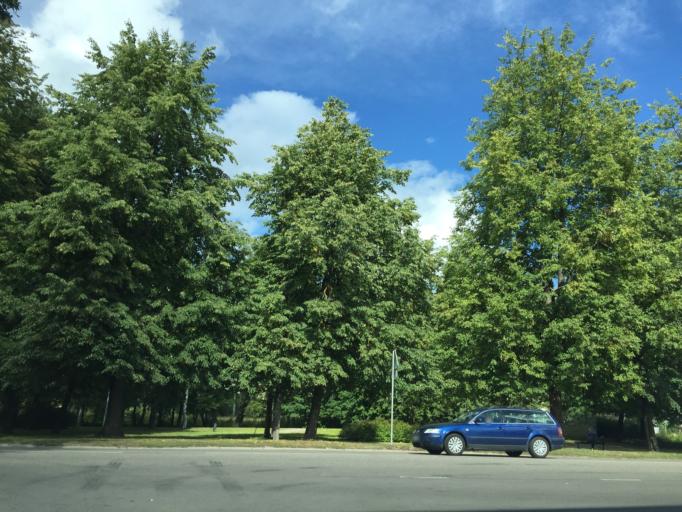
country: LV
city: Tireli
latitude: 56.9457
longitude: 23.6146
